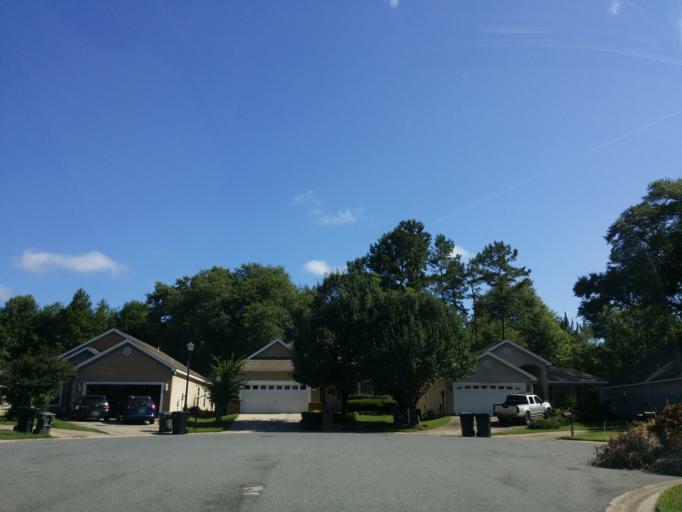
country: US
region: Florida
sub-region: Leon County
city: Tallahassee
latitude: 30.4587
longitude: -84.2145
